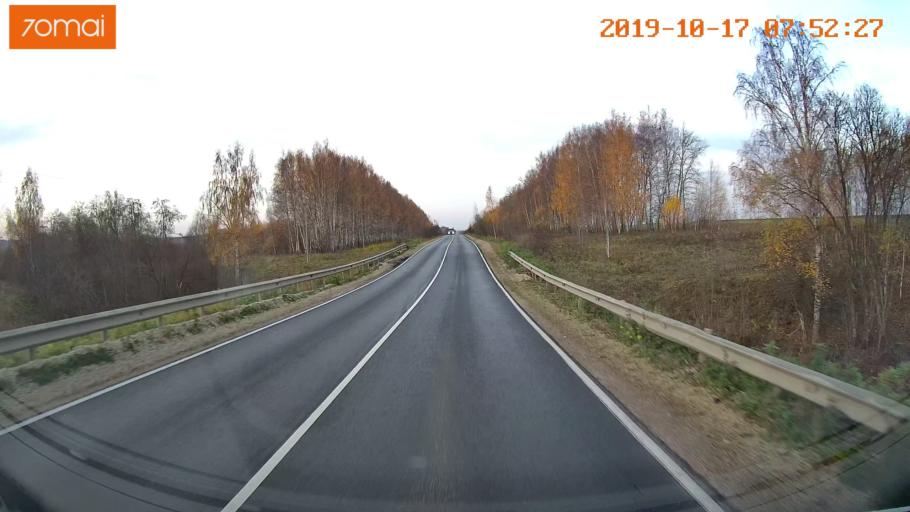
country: RU
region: Vladimir
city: Yur'yev-Pol'skiy
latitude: 56.4724
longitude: 39.6402
